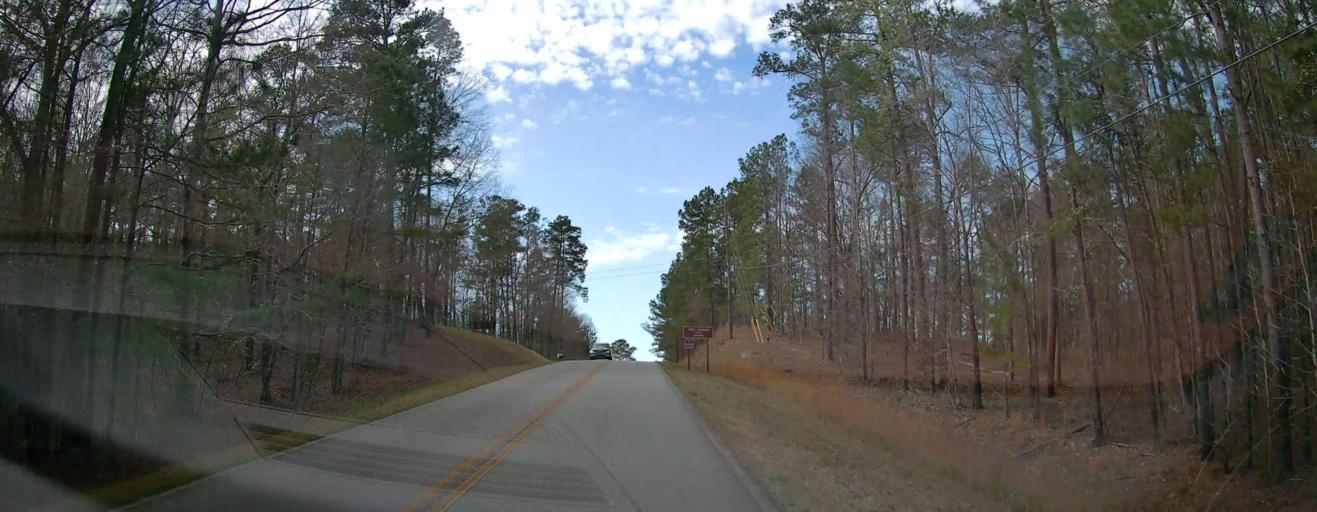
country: US
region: Georgia
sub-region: Jones County
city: Gray
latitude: 33.0533
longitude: -83.7209
